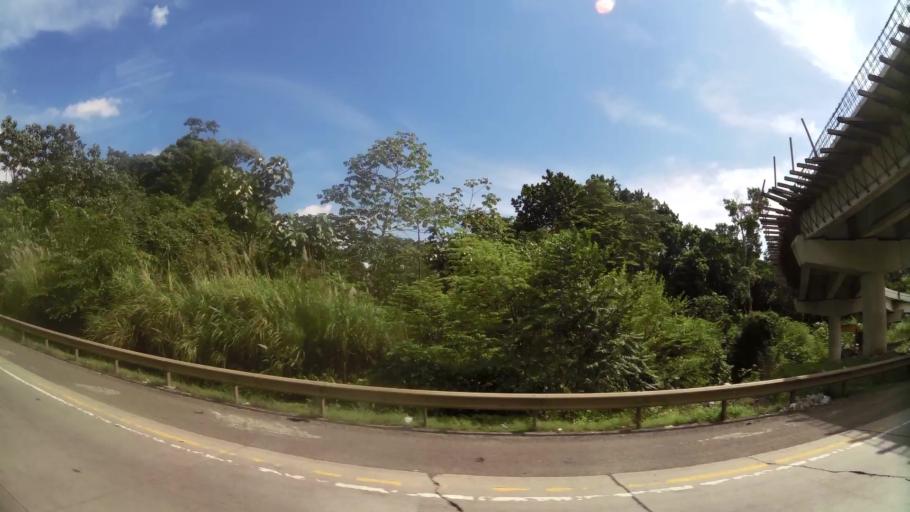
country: PA
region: Panama
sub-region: Distrito de Panama
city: Paraiso
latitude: 9.0354
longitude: -79.5773
